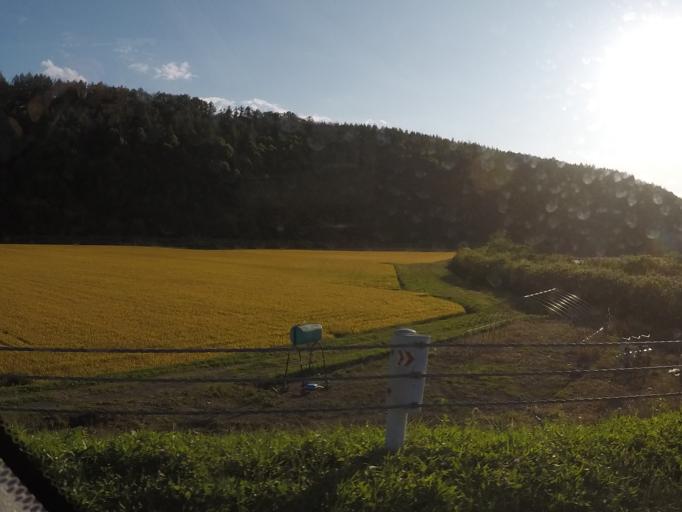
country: JP
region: Hokkaido
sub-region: Asahikawa-shi
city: Asahikawa
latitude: 43.6259
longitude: 142.5351
